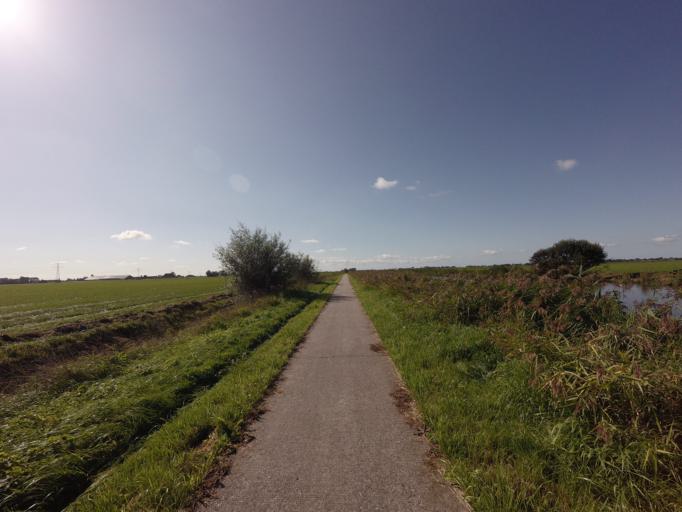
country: NL
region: Friesland
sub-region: Gemeente Boarnsterhim
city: Reduzum
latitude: 53.1407
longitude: 5.7630
